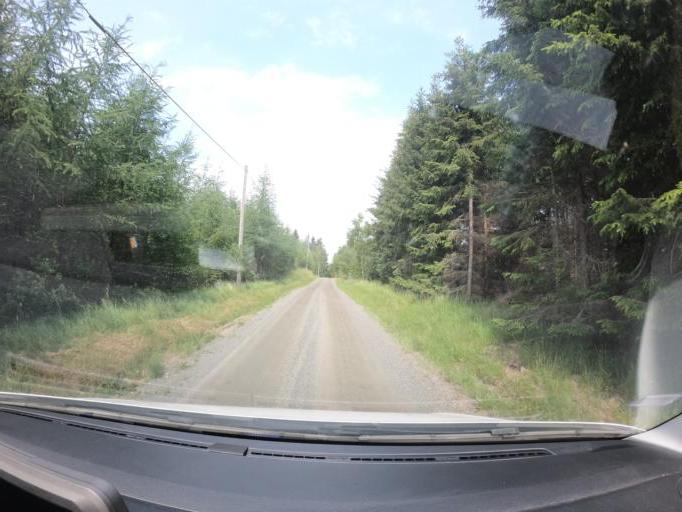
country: SE
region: Skane
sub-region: Hassleholms Kommun
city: Bjarnum
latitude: 56.2701
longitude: 13.6368
